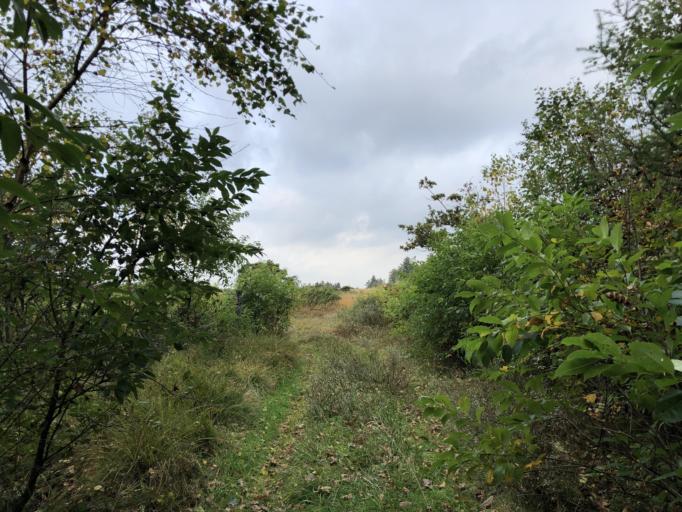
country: DK
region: Central Jutland
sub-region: Holstebro Kommune
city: Ulfborg
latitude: 56.2158
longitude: 8.4293
